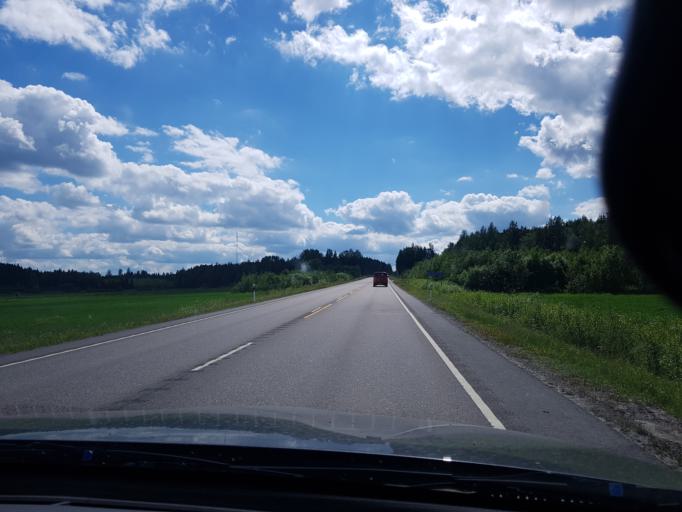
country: FI
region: Haeme
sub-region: Haemeenlinna
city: Parola
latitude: 61.0950
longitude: 24.4039
